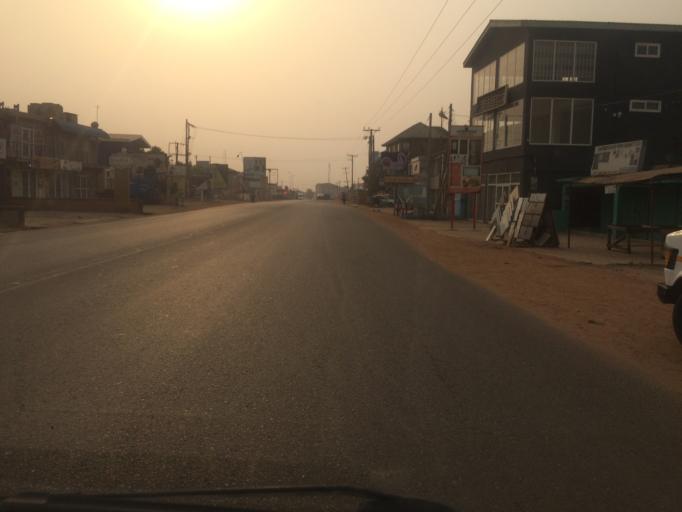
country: GH
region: Greater Accra
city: Nungua
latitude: 5.6314
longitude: -0.0942
